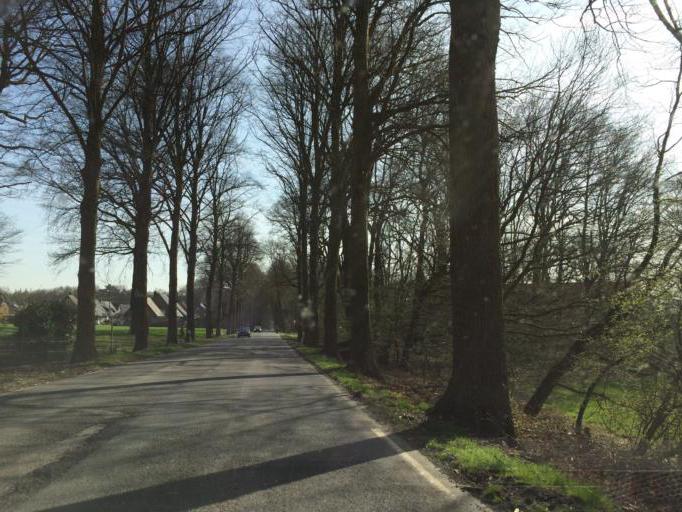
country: DE
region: North Rhine-Westphalia
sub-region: Regierungsbezirk Munster
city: Haltern
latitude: 51.7323
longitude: 7.1063
